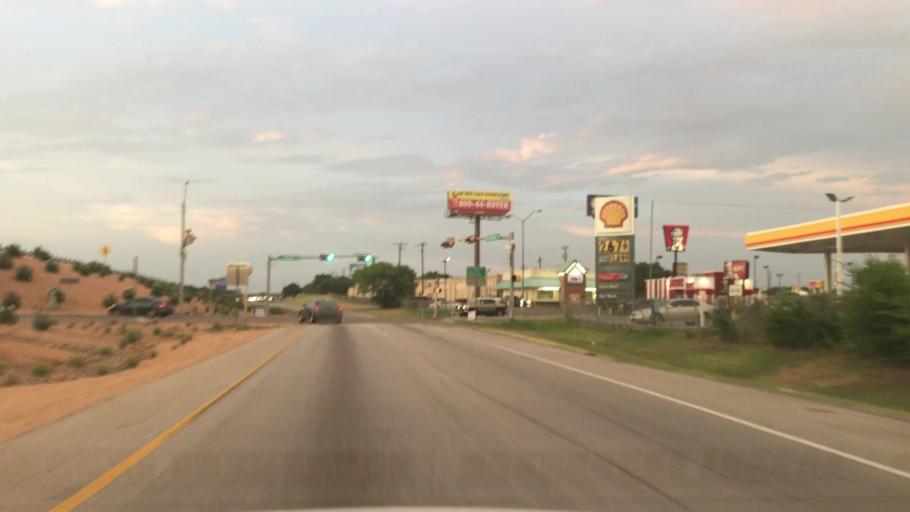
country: US
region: Texas
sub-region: Dallas County
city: Balch Springs
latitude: 32.7189
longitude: -96.6159
